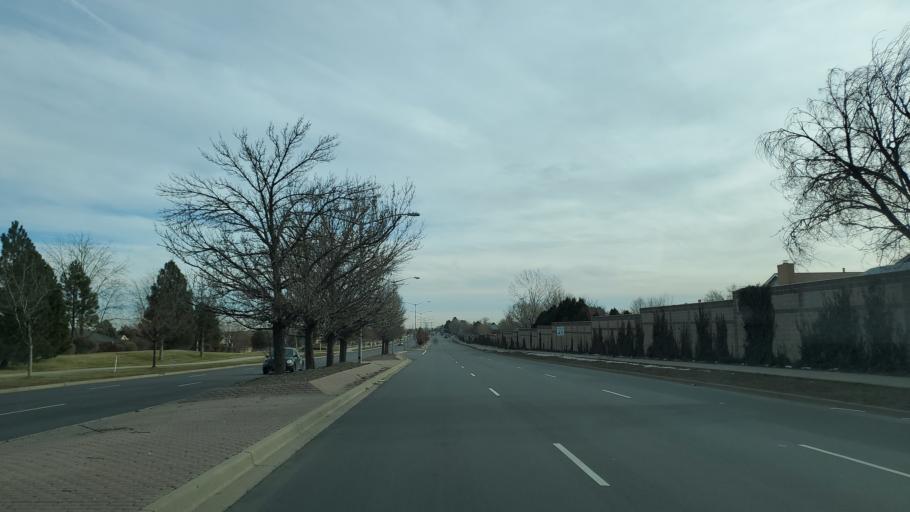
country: US
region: Colorado
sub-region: Adams County
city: Northglenn
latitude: 39.9138
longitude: -104.9515
